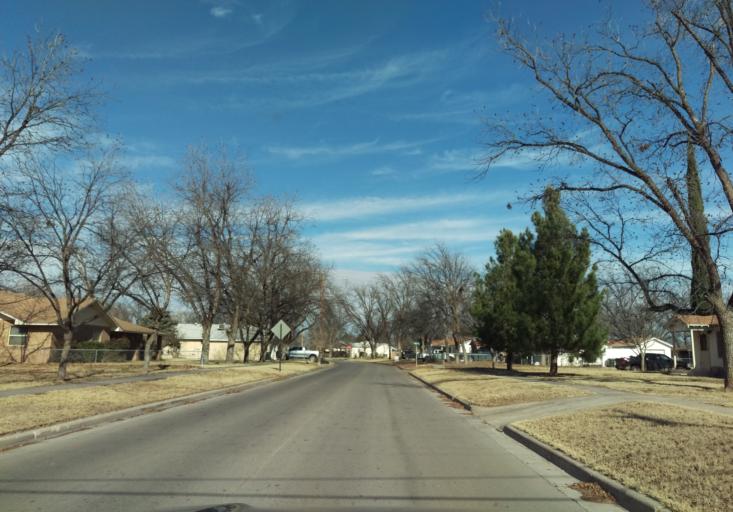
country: US
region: New Mexico
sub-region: Eddy County
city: Carlsbad
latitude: 32.4321
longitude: -104.2263
